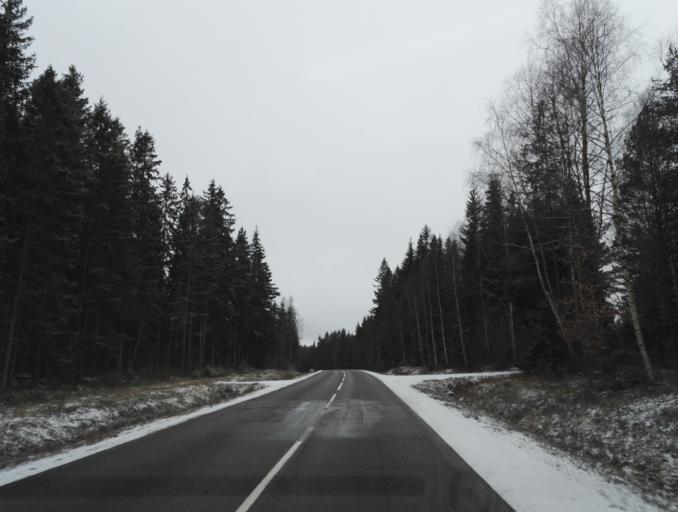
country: SE
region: Kronoberg
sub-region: Tingsryds Kommun
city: Tingsryd
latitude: 56.5550
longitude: 15.0416
